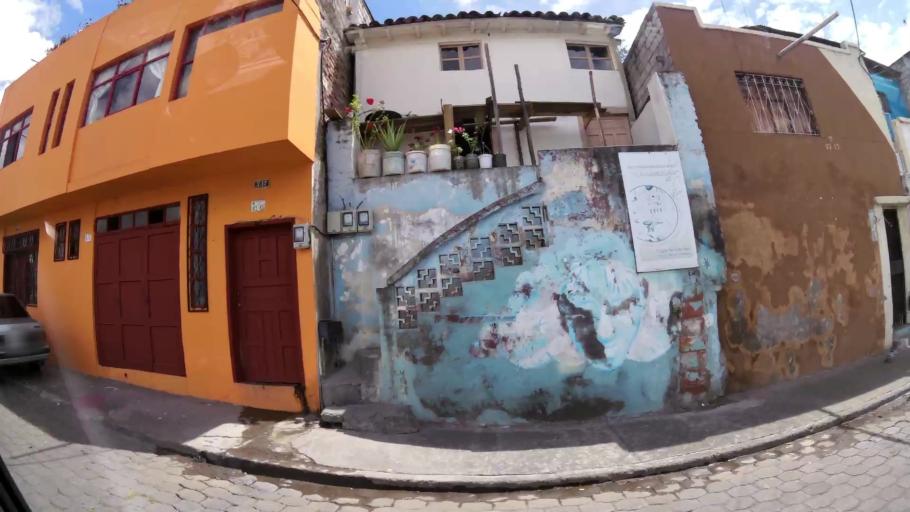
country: EC
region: Tungurahua
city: Ambato
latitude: -1.2474
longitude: -78.6293
